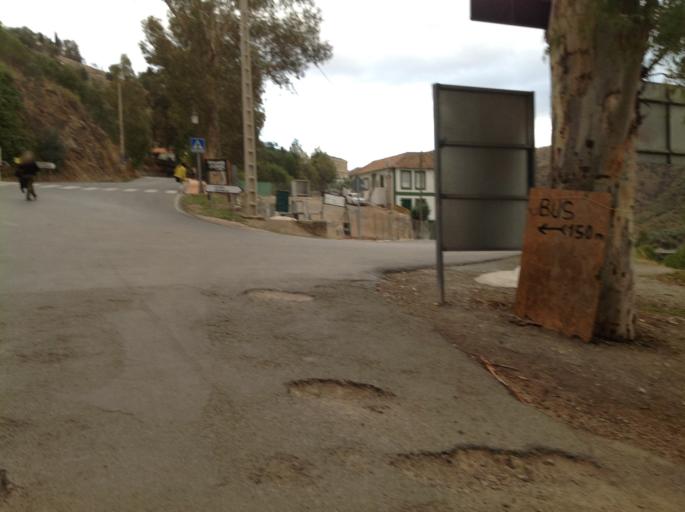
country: ES
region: Andalusia
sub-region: Provincia de Malaga
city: Carratraca
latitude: 36.9089
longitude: -4.7606
